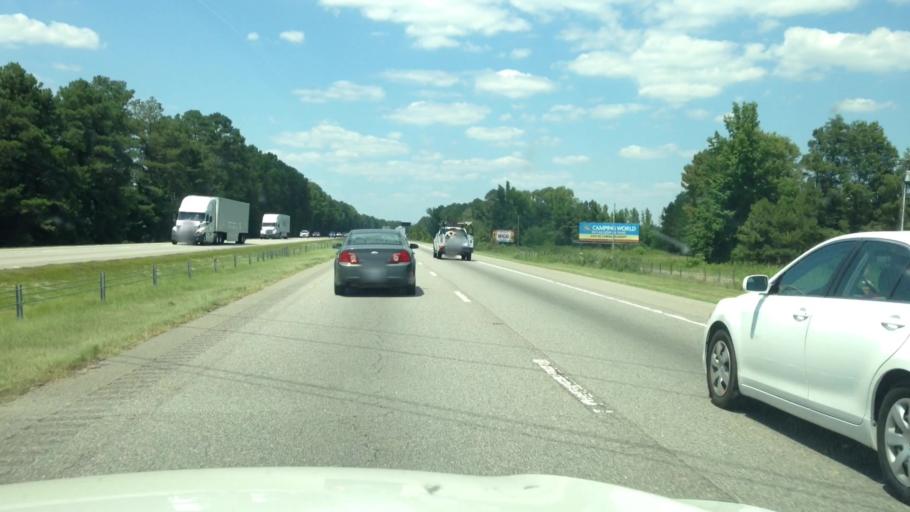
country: US
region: North Carolina
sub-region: Cumberland County
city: Hope Mills
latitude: 34.8939
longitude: -78.9594
